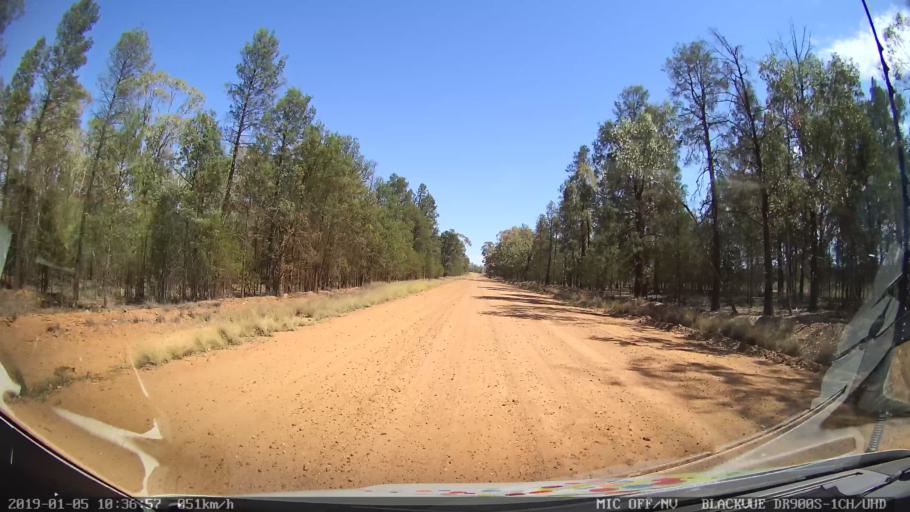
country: AU
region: New South Wales
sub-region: Gilgandra
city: Gilgandra
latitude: -31.4783
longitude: 148.9233
